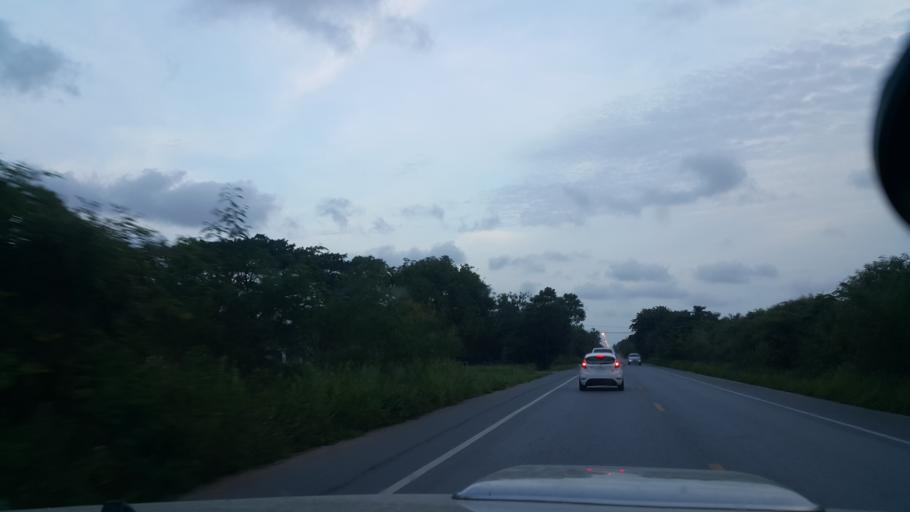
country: TH
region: Rayong
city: Ban Chang
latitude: 12.7202
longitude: 100.9909
